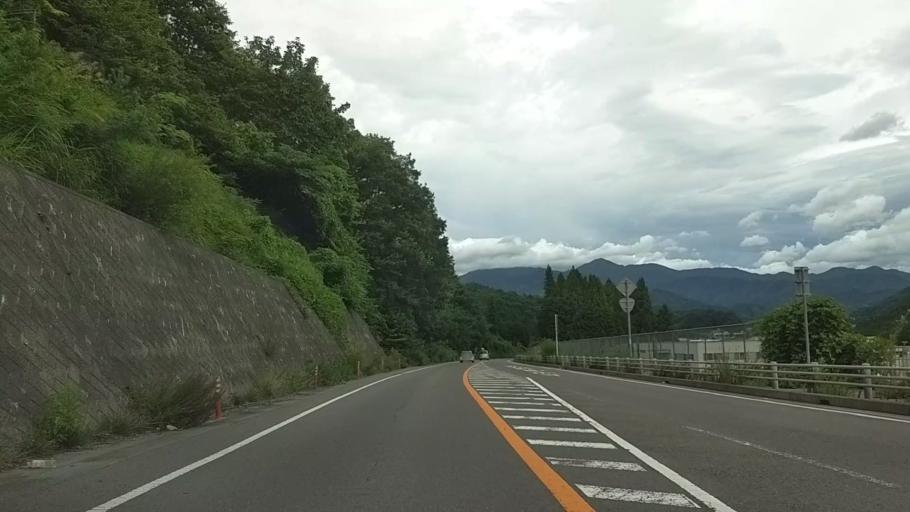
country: JP
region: Yamanashi
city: Otsuki
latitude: 35.5629
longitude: 138.9340
